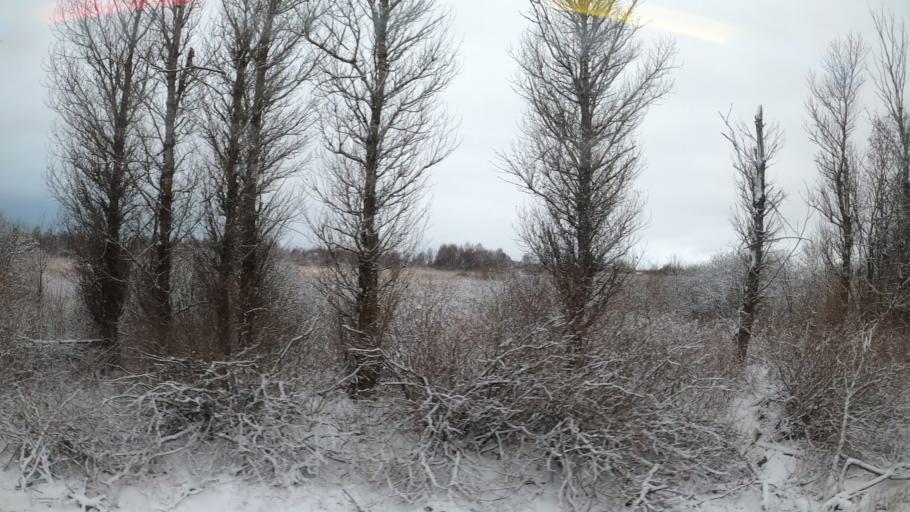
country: RU
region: Jaroslavl
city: Pereslavl'-Zalesskiy
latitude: 56.7125
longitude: 38.9112
